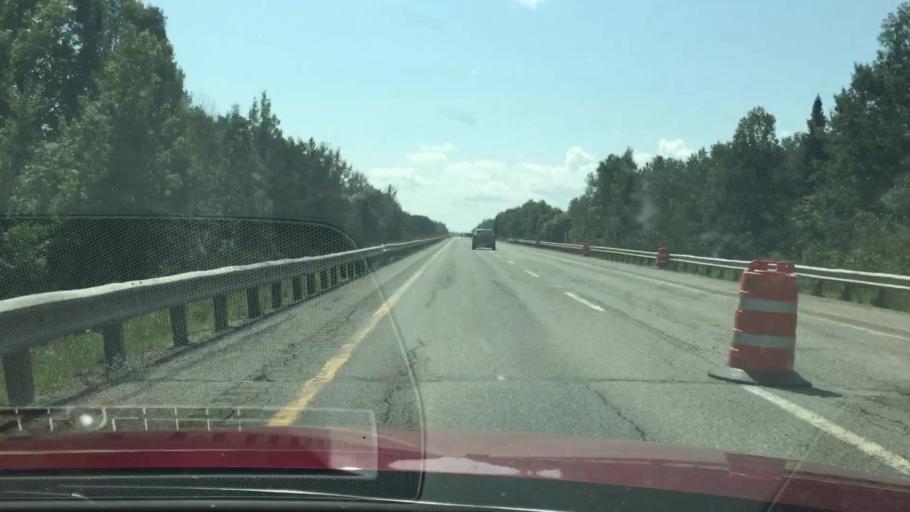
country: US
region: Maine
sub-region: Penobscot County
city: Patten
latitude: 45.8665
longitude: -68.4173
